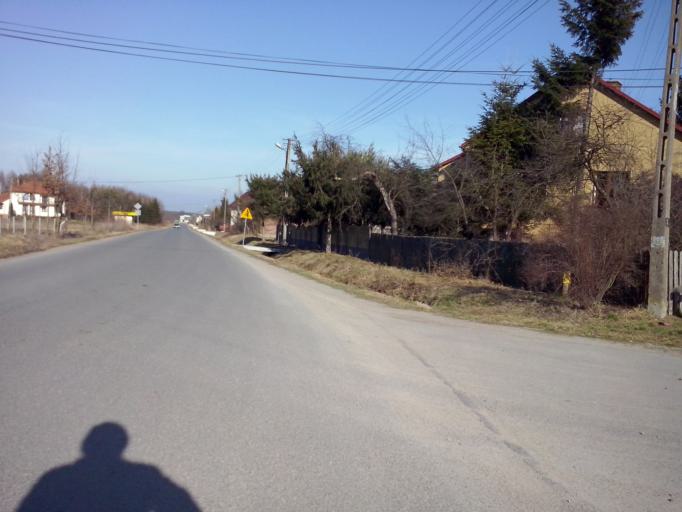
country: PL
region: Subcarpathian Voivodeship
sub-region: Powiat nizanski
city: Krzeszow
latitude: 50.4144
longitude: 22.3752
